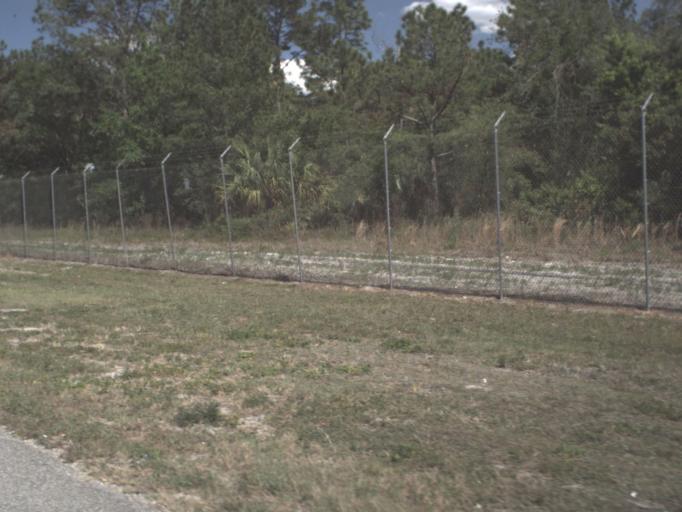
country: US
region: Florida
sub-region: Lake County
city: Mount Plymouth
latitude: 28.8156
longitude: -81.4964
